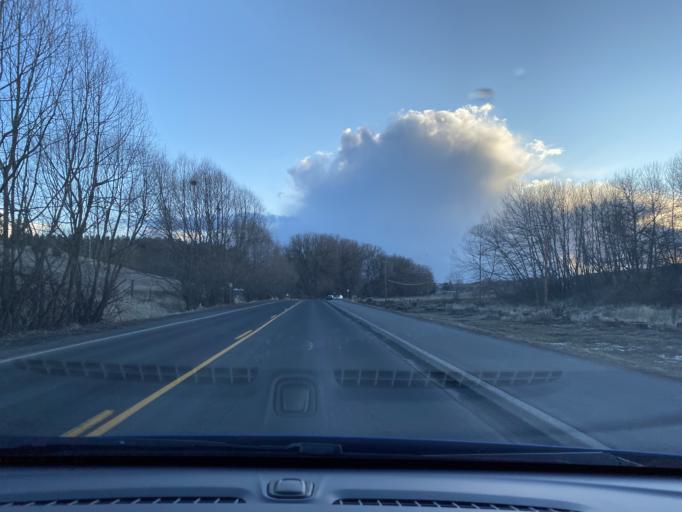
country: US
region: Washington
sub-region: Whitman County
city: Pullman
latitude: 46.7343
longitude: -117.1336
